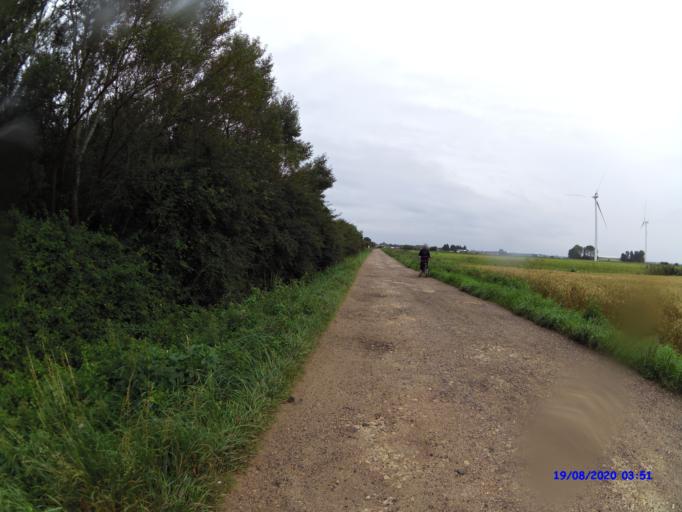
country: GB
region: England
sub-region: Cambridgeshire
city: Ramsey
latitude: 52.4646
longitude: -0.1109
